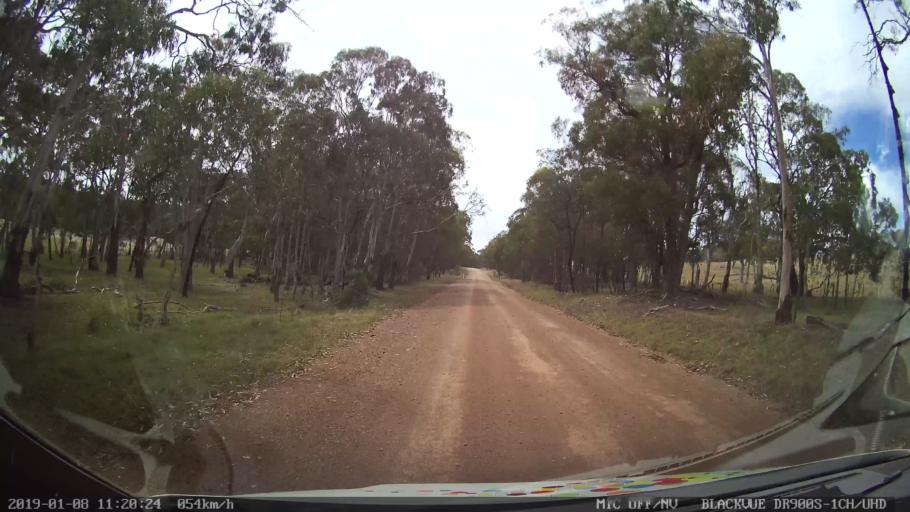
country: AU
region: New South Wales
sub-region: Guyra
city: Guyra
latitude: -30.2304
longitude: 151.5611
